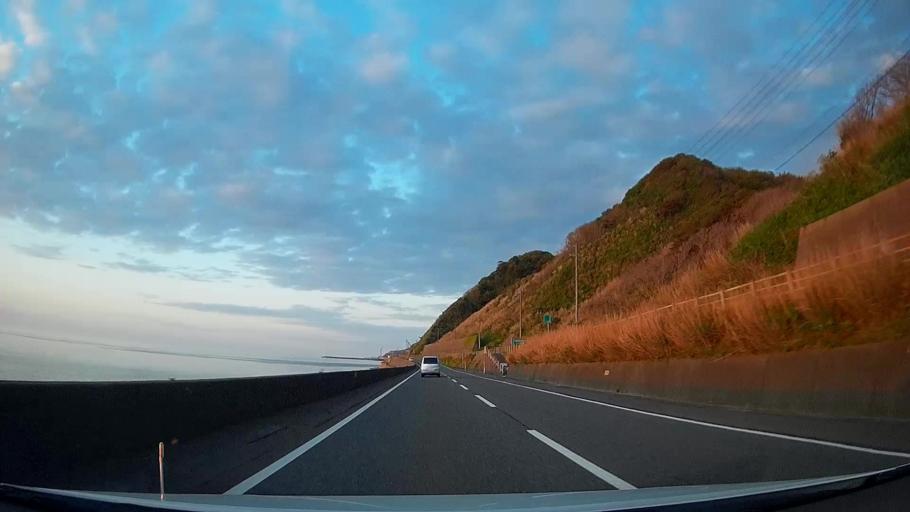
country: JP
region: Niigata
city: Joetsu
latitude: 37.1458
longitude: 138.0654
